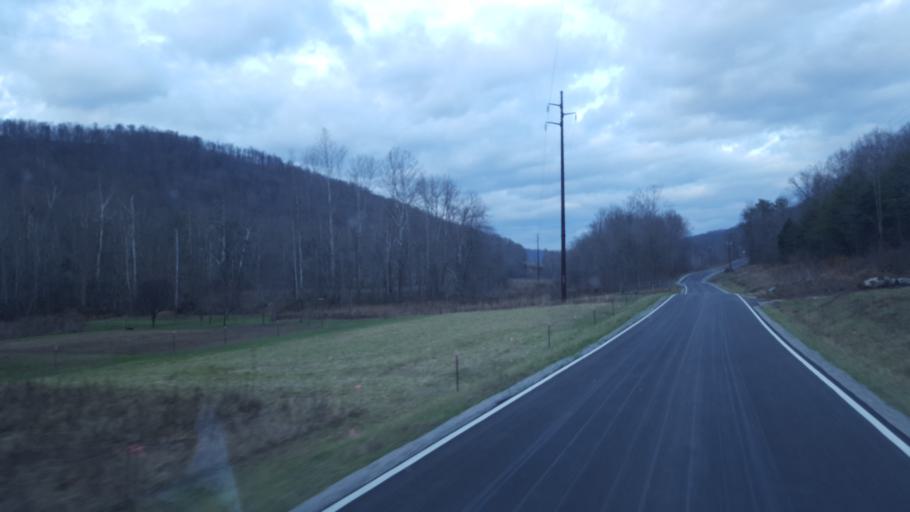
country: US
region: Kentucky
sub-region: Lewis County
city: Vanceburg
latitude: 38.5129
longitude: -83.4817
